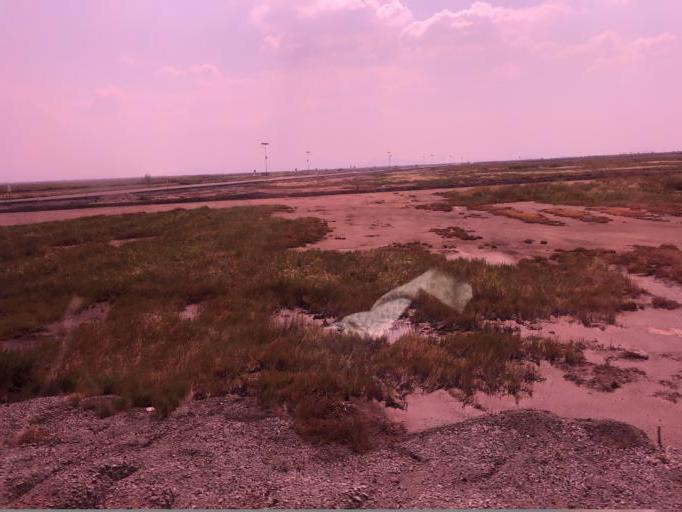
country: MX
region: Mexico
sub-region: Atenco
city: Colonia el Salado
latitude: 19.5518
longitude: -98.9855
